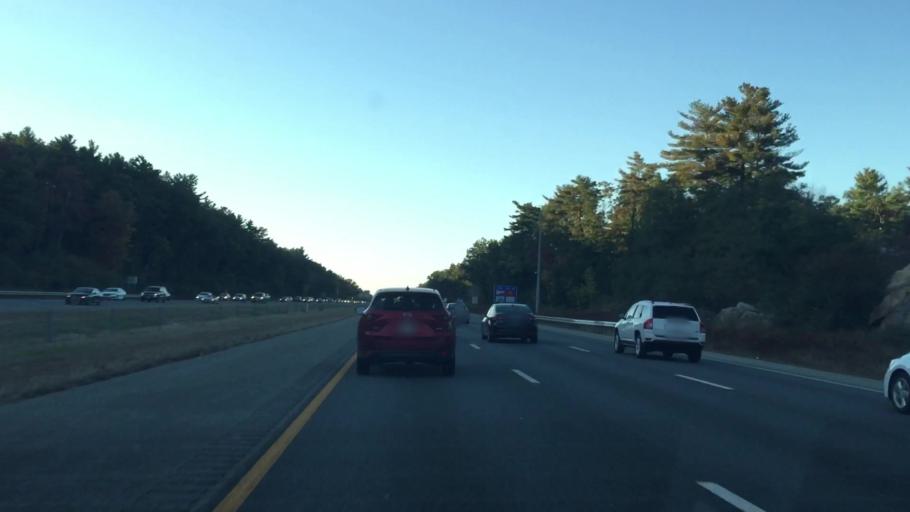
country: US
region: Massachusetts
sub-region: Middlesex County
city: Billerica
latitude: 42.5501
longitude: -71.2891
